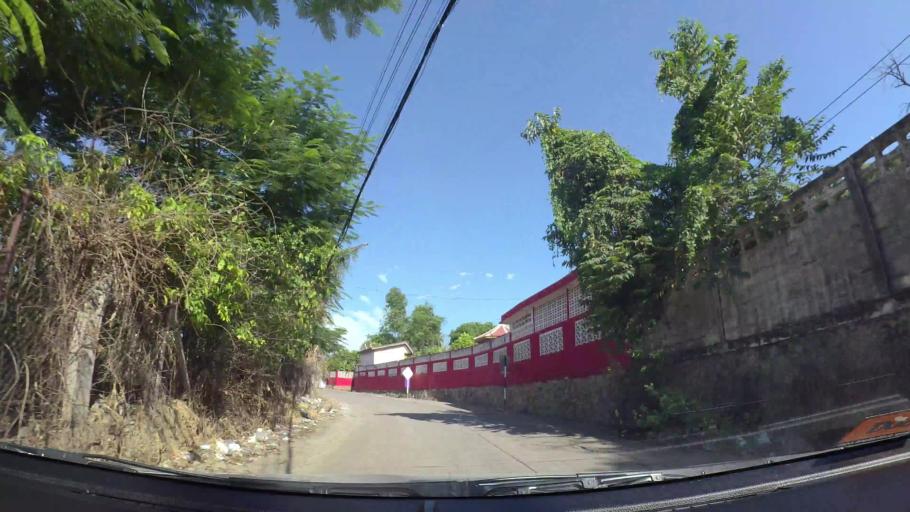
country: TH
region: Chon Buri
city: Si Racha
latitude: 13.1596
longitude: 100.9271
